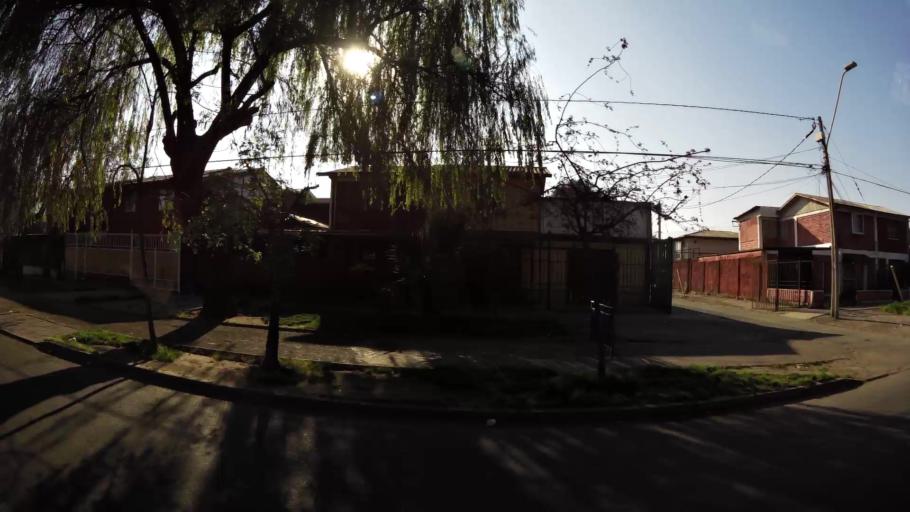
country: CL
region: Santiago Metropolitan
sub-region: Provincia de Santiago
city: Santiago
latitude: -33.3800
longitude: -70.6576
